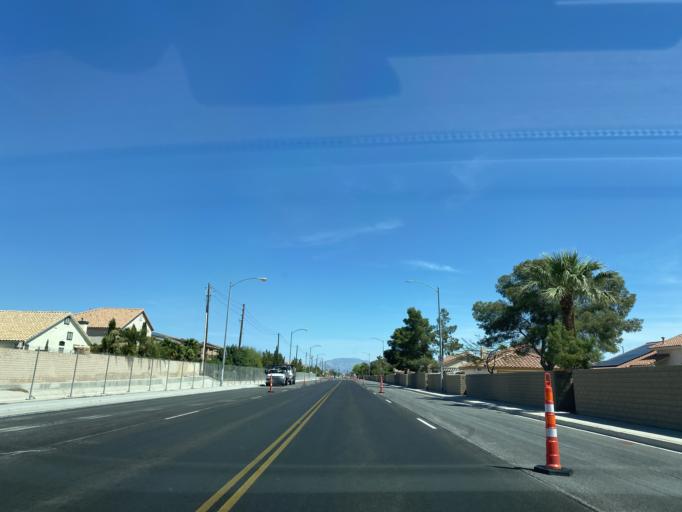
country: US
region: Nevada
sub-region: Clark County
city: Spring Valley
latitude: 36.1025
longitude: -115.2610
